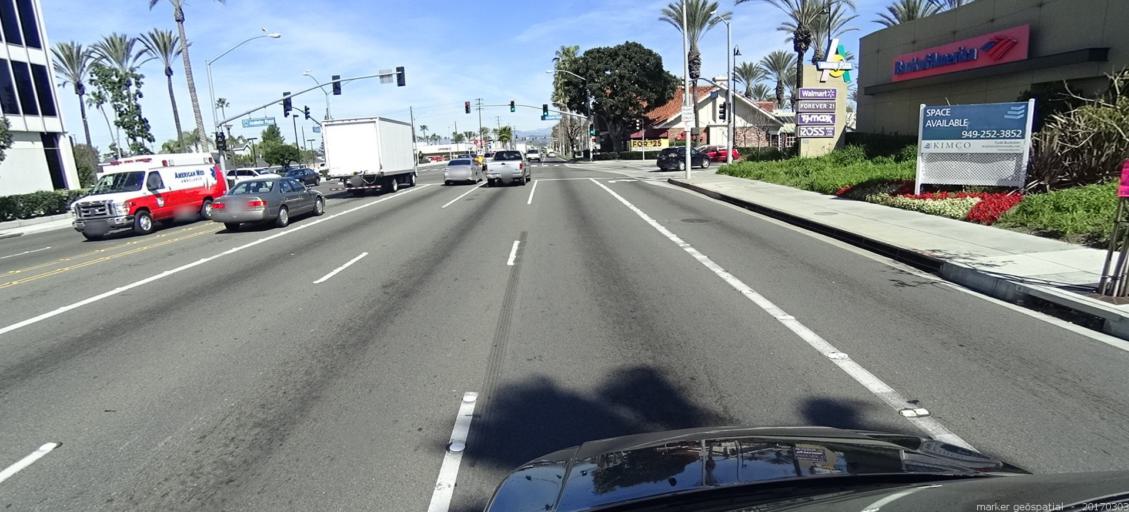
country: US
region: California
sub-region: Orange County
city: Anaheim
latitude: 33.8379
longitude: -117.9415
